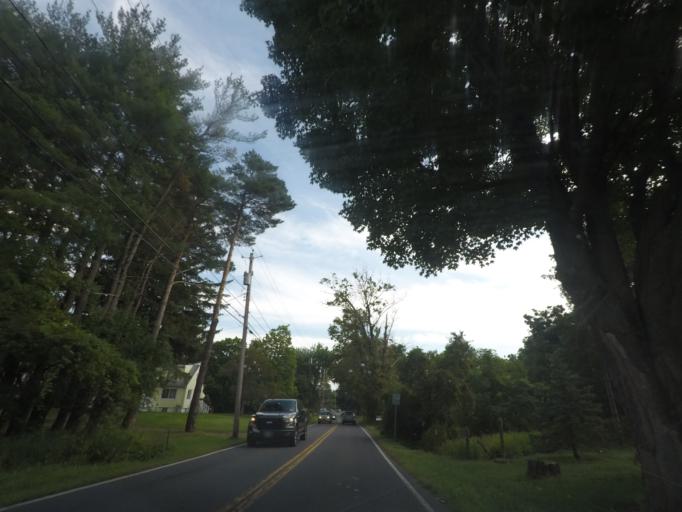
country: US
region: New York
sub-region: Albany County
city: Delmar
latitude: 42.6193
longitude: -73.7977
